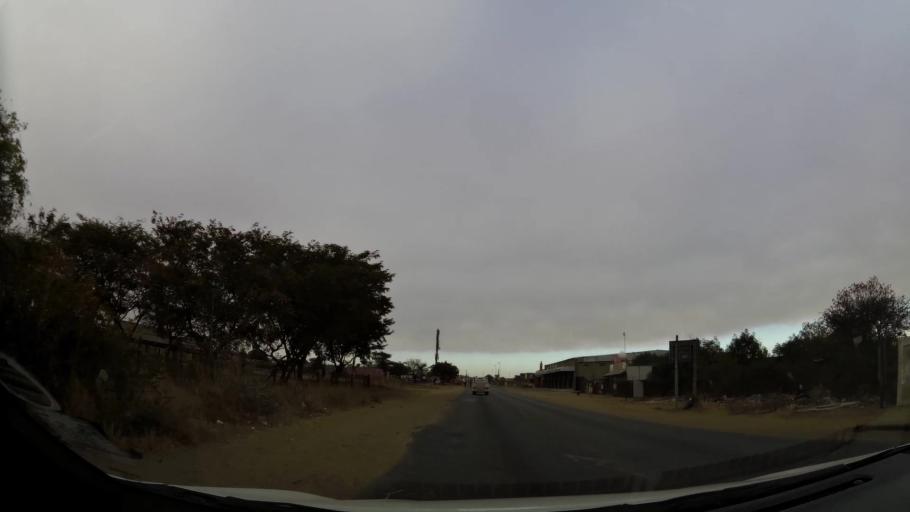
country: ZA
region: Limpopo
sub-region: Capricorn District Municipality
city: Polokwane
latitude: -23.8325
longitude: 29.3795
